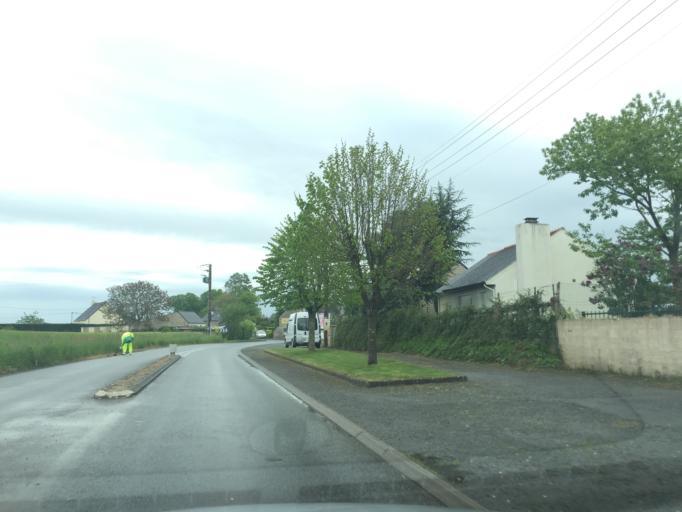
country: FR
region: Brittany
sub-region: Departement des Cotes-d'Armor
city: Crehen
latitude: 48.5512
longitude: -2.2342
